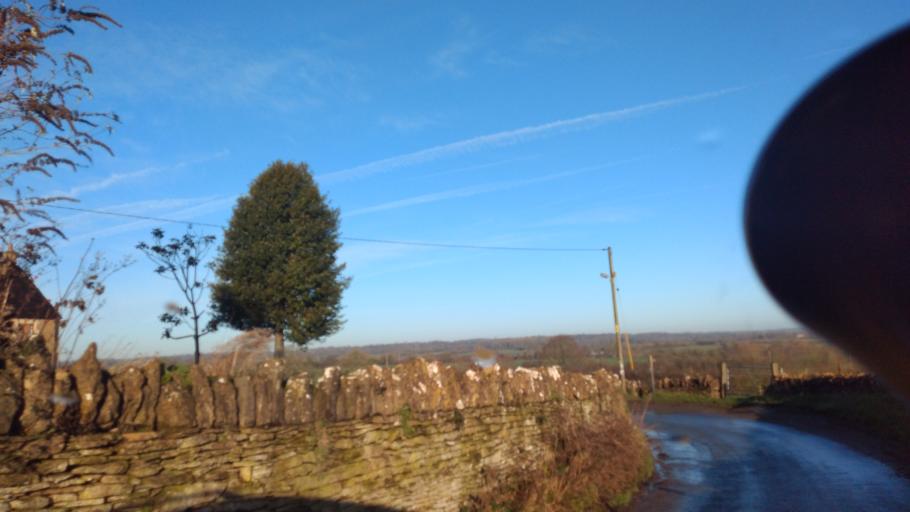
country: GB
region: England
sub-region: Wiltshire
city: Corsham
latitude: 51.4139
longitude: -2.1617
